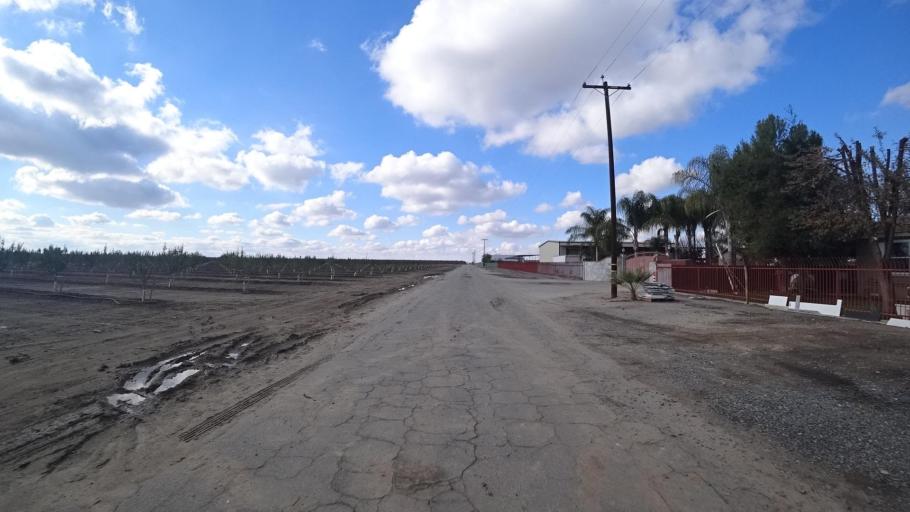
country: US
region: California
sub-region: Kern County
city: McFarland
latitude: 35.6671
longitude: -119.2550
